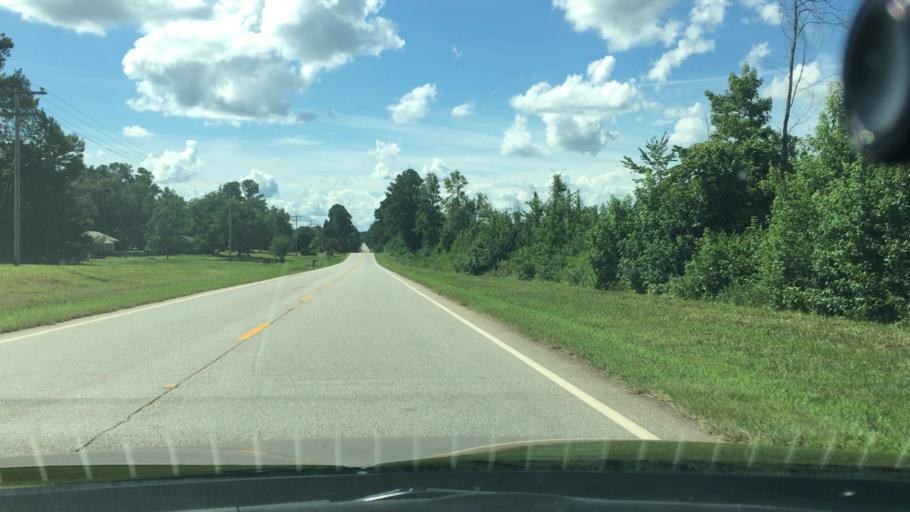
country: US
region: Georgia
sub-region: Jasper County
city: Monticello
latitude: 33.3061
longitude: -83.7360
